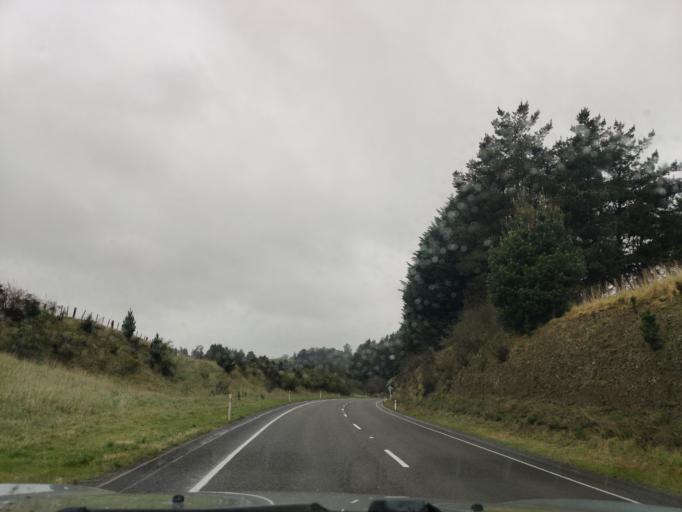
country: NZ
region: Manawatu-Wanganui
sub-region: Palmerston North City
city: Palmerston North
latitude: -40.0546
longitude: 176.2334
